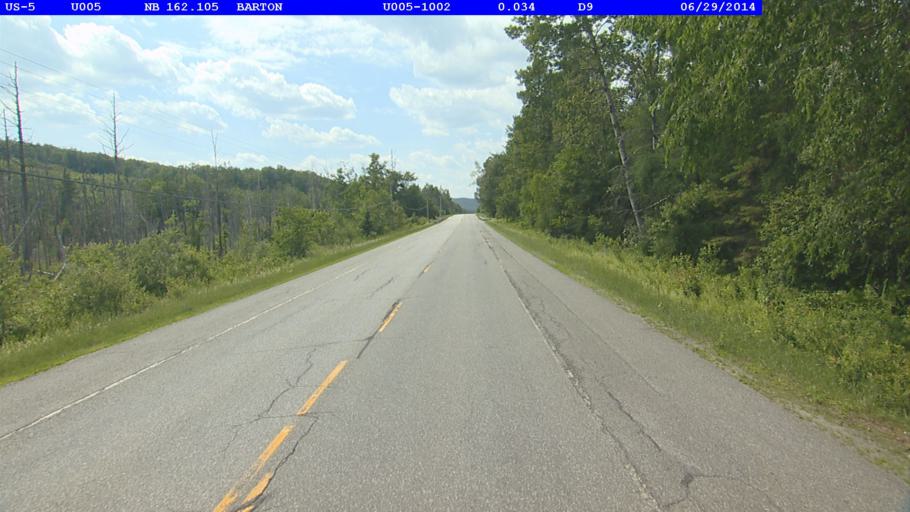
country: US
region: Vermont
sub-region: Caledonia County
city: Lyndonville
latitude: 44.7003
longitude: -72.0958
